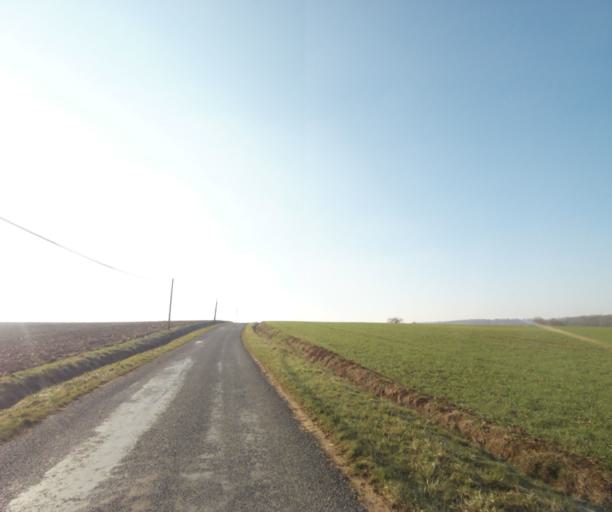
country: FR
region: Champagne-Ardenne
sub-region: Departement de la Haute-Marne
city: Bienville
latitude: 48.5307
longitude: 5.0058
